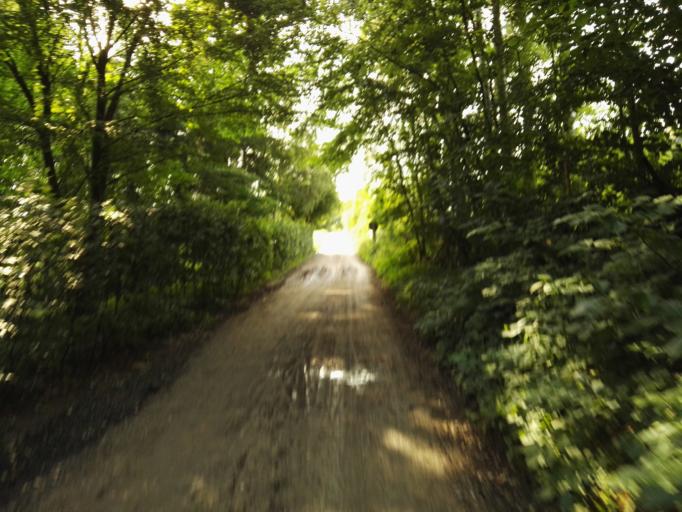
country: DK
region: Capital Region
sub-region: Ballerup Kommune
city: Ballerup
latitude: 55.7494
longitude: 12.3624
